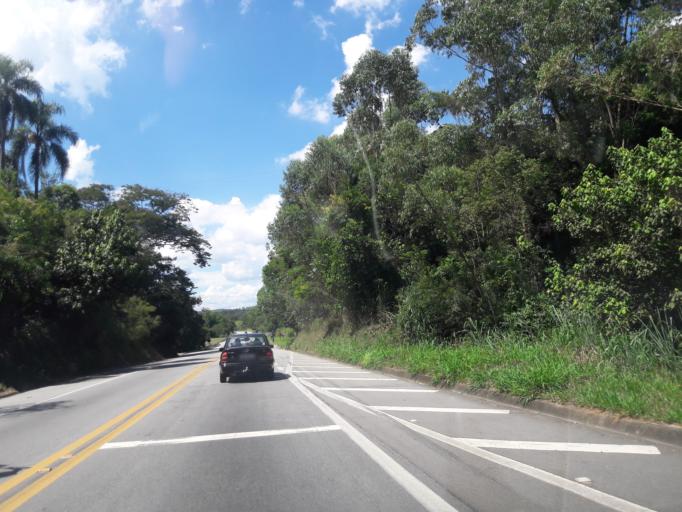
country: BR
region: Sao Paulo
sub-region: Cajamar
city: Cajamar
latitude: -23.3136
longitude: -46.8190
